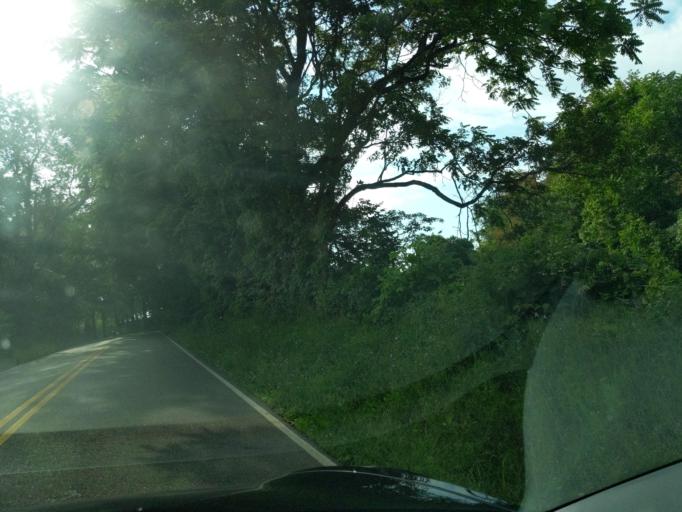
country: US
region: Ohio
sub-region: Fairfield County
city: Lancaster
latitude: 39.5733
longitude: -82.5822
